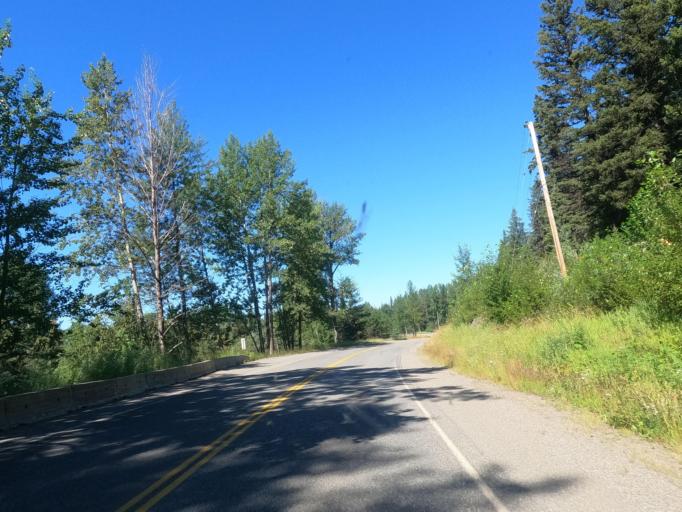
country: CA
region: British Columbia
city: Quesnel
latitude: 53.0420
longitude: -122.2493
